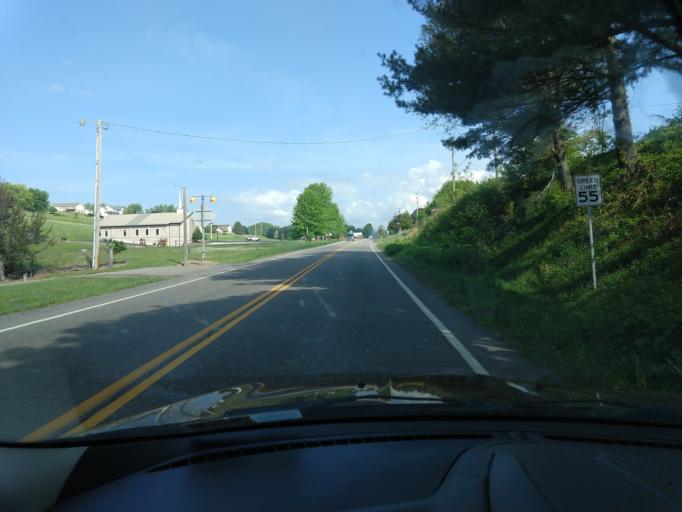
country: US
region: Virginia
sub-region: Russell County
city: Honaker
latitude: 36.9618
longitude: -81.9338
